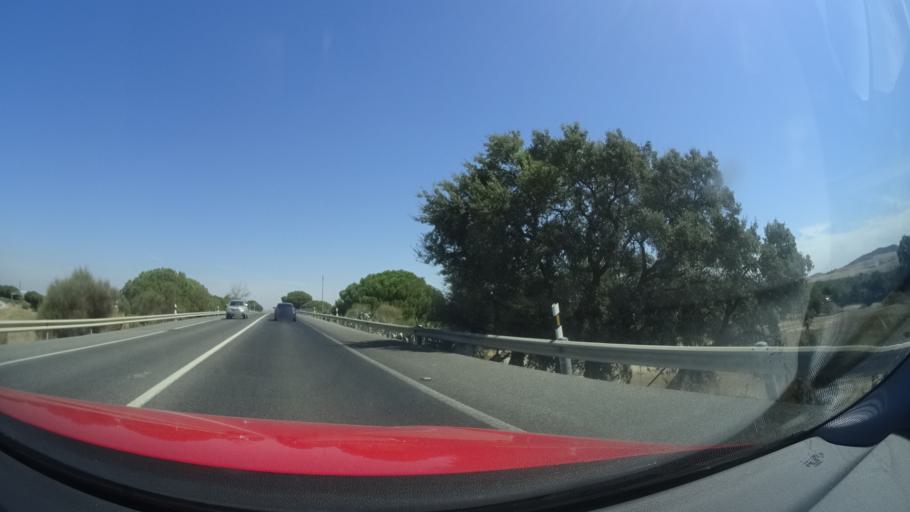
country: ES
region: Andalusia
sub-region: Provincia de Sevilla
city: Las Cabezas de San Juan
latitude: 36.9069
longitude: -5.9709
